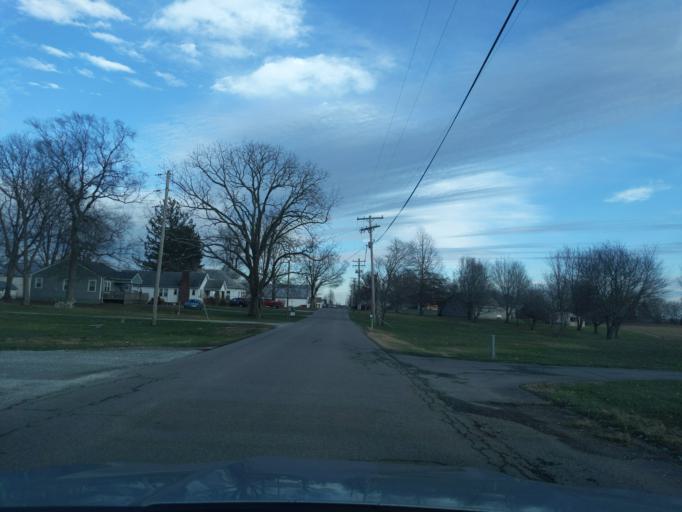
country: US
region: Indiana
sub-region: Decatur County
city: Westport
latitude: 39.2347
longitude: -85.5679
